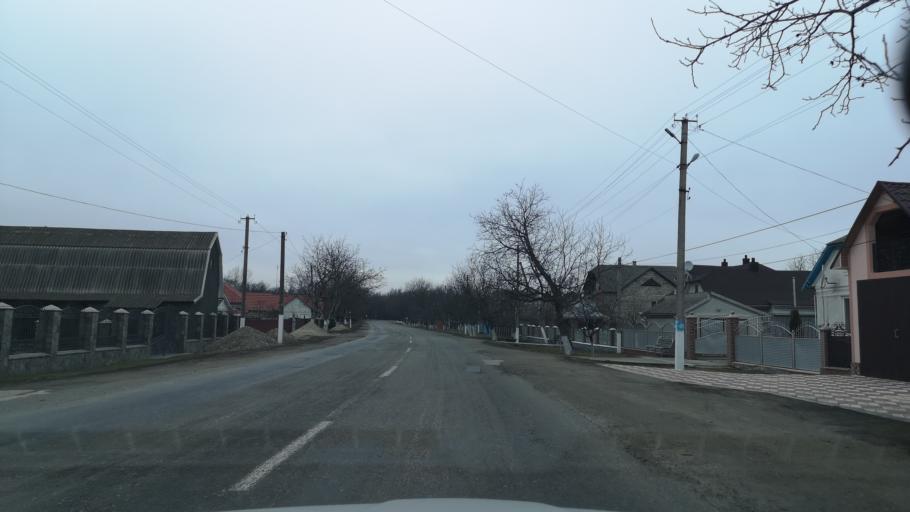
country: RO
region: Botosani
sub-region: Comuna Hudesti
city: Alba
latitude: 48.2208
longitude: 26.4773
